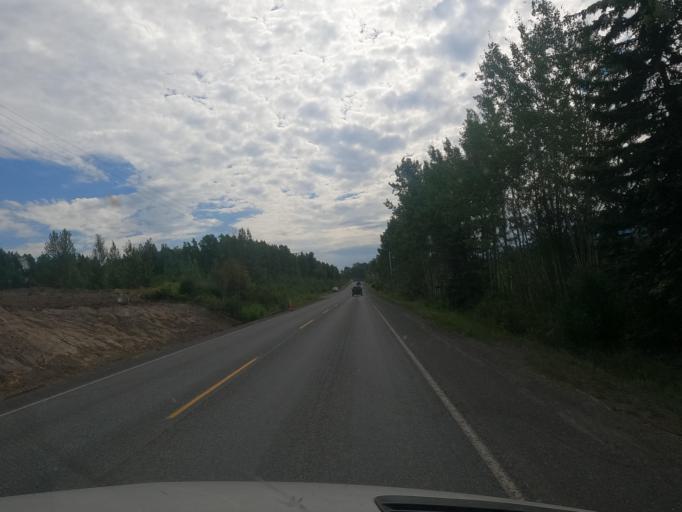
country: CA
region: British Columbia
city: Smithers
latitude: 54.8582
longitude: -127.2273
